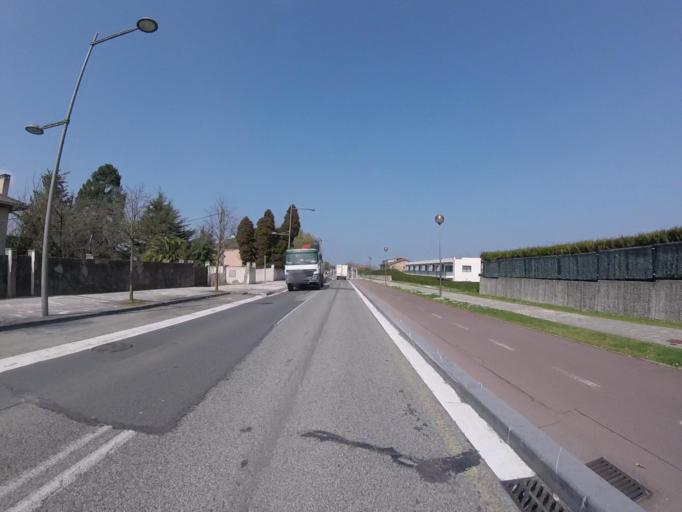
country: ES
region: Basque Country
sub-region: Provincia de Guipuzcoa
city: San Sebastian
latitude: 43.2906
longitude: -1.9904
